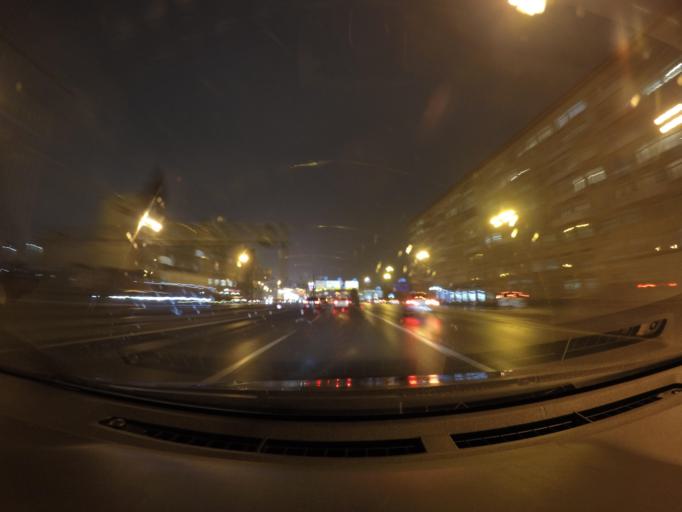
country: RU
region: Moscow
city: Lefortovo
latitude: 55.7767
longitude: 37.6815
